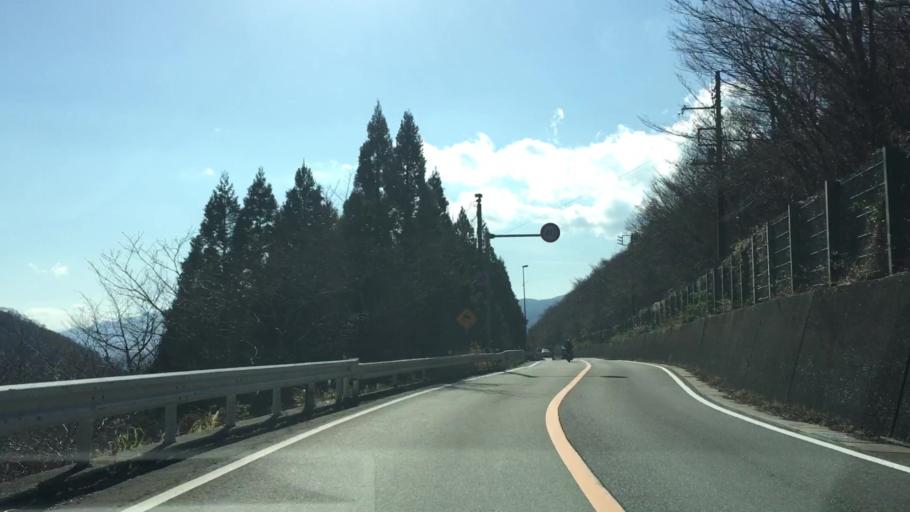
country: JP
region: Shizuoka
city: Gotemba
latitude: 35.3897
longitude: 138.8627
